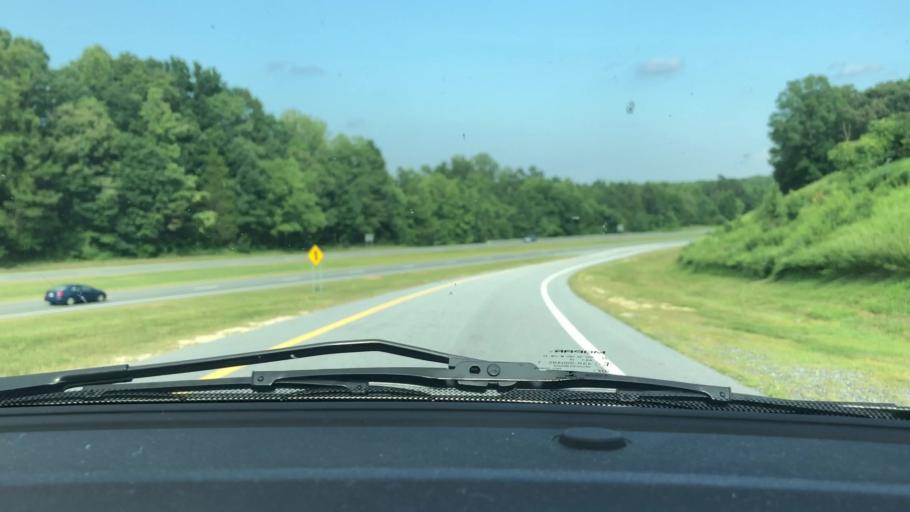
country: US
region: North Carolina
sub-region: Guilford County
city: Forest Oaks
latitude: 35.9618
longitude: -79.7023
